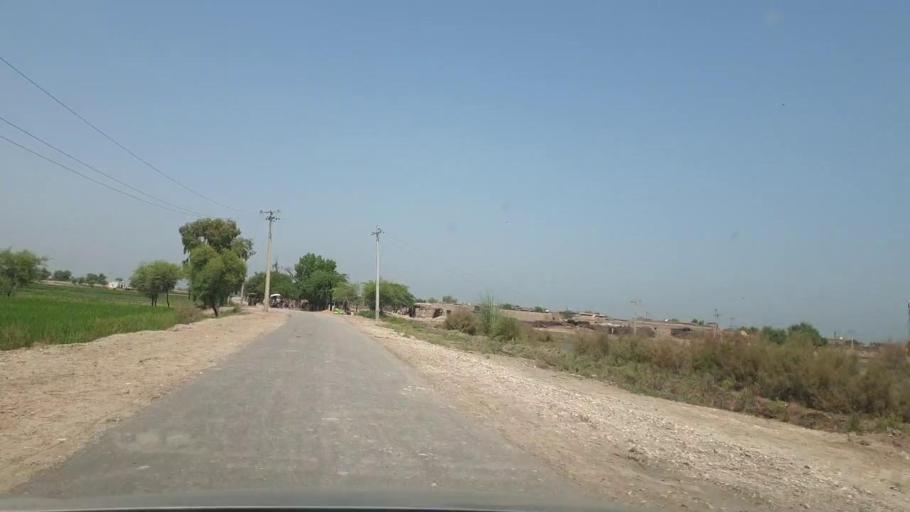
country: PK
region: Sindh
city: Warah
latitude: 27.4787
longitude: 67.7567
